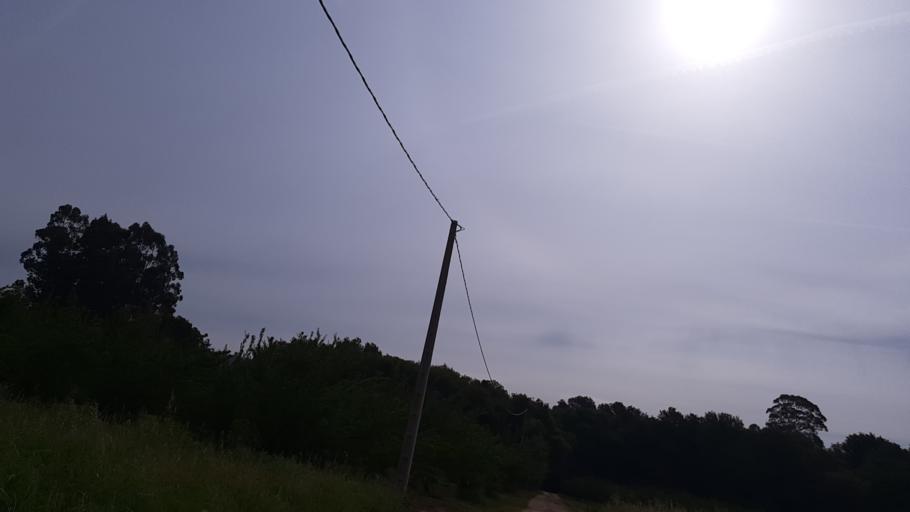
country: ES
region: Galicia
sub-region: Provincia de Pontevedra
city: O Rosal
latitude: 41.9246
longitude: -8.8284
